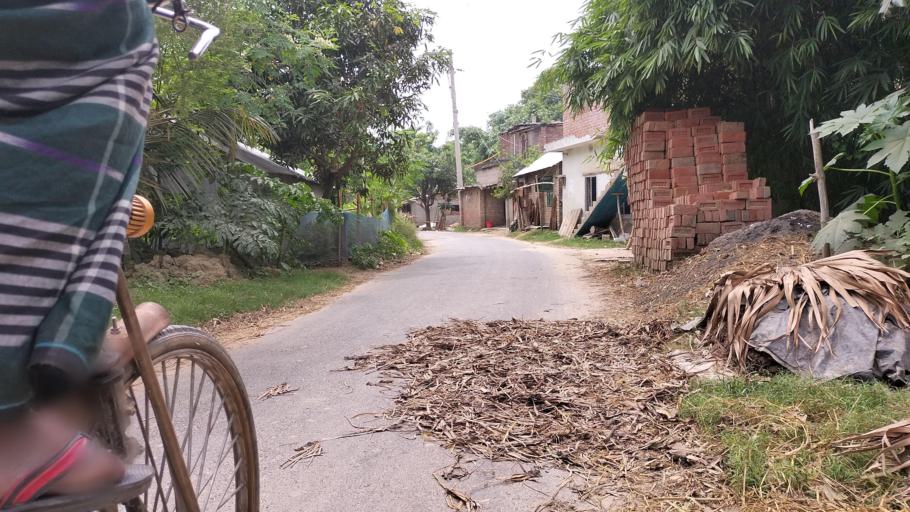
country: BD
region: Rajshahi
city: Rajshahi
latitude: 24.5150
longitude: 88.6294
